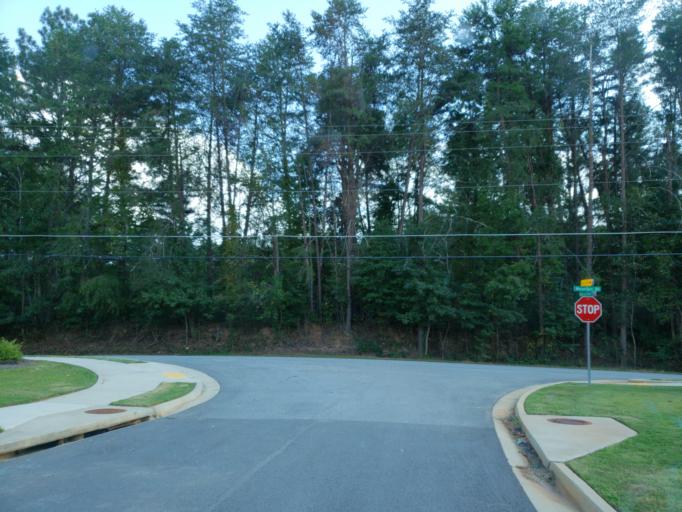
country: US
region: Georgia
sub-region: Cherokee County
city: Woodstock
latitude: 34.0605
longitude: -84.4435
